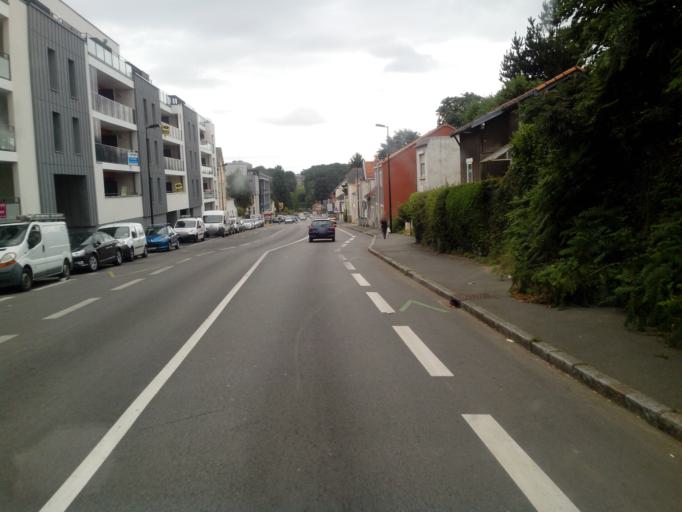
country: FR
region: Pays de la Loire
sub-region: Departement de la Loire-Atlantique
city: Nantes
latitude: 47.2520
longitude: -1.5764
